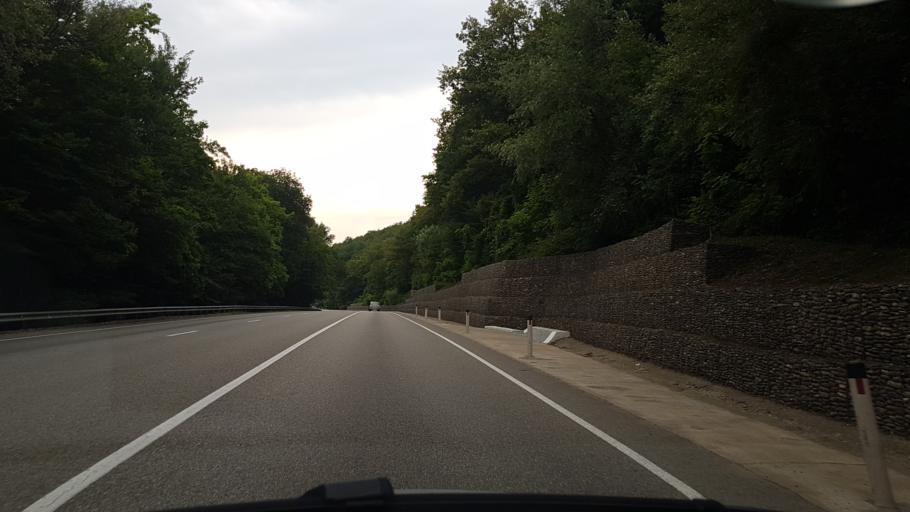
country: RU
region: Krasnodarskiy
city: Lermontovo
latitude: 44.4645
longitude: 38.8613
